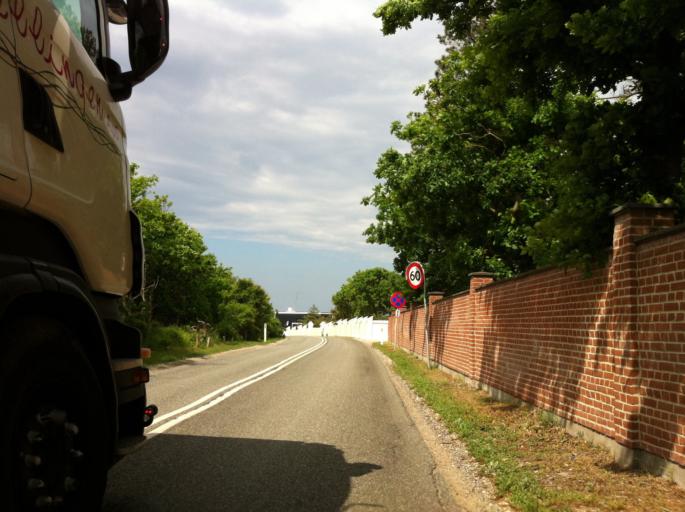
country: DK
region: Capital Region
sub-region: Gribskov Kommune
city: Helsinge
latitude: 56.1068
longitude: 12.1810
